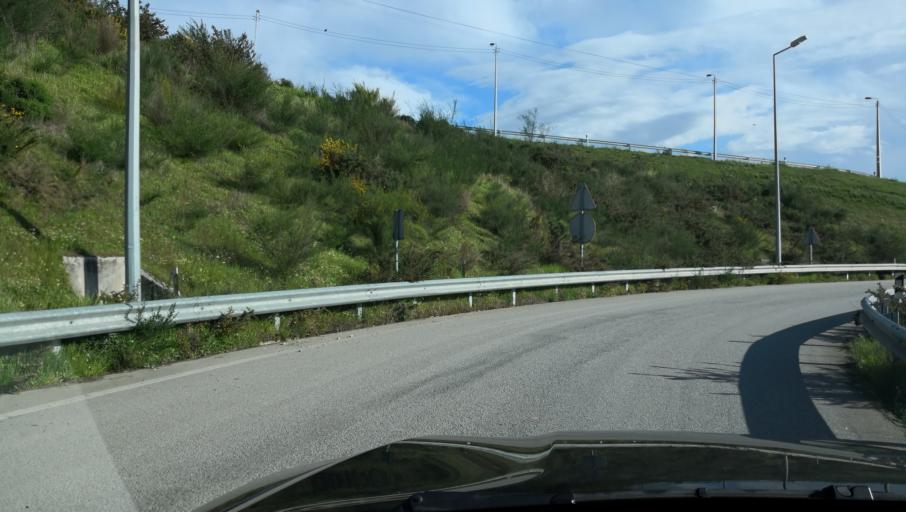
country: PT
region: Vila Real
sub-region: Vila Real
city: Vila Real
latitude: 41.2552
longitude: -7.7132
